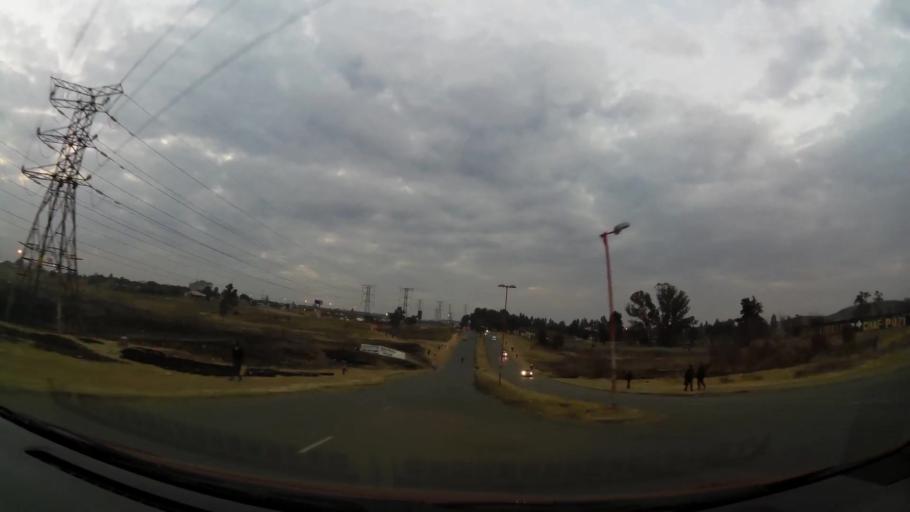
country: ZA
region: Gauteng
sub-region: City of Johannesburg Metropolitan Municipality
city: Soweto
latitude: -26.2539
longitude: 27.9283
